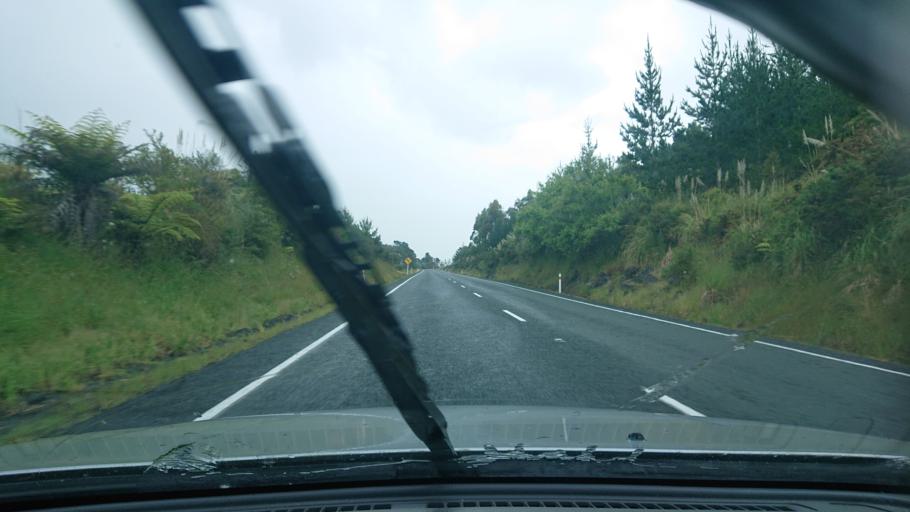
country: NZ
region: Auckland
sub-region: Auckland
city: Wellsford
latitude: -36.3291
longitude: 174.4705
